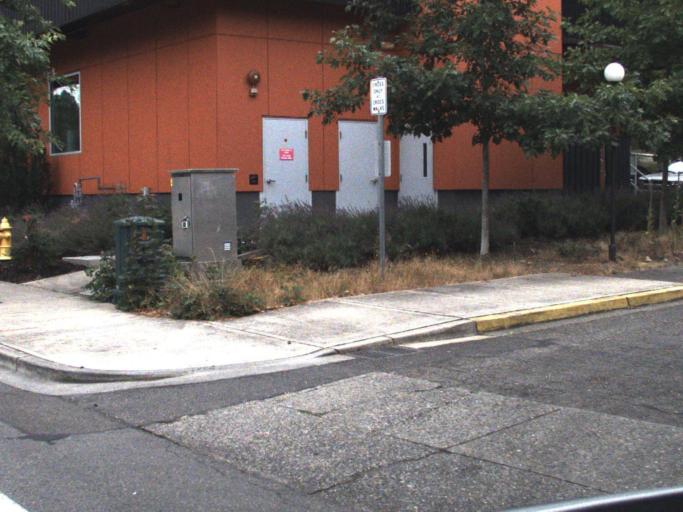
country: US
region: Washington
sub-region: King County
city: Redmond
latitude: 47.6795
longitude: -122.1216
